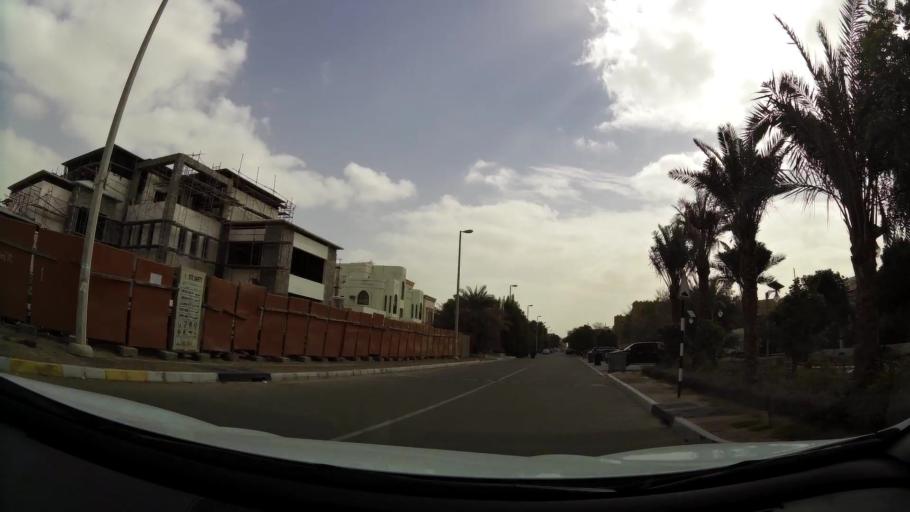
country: AE
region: Abu Dhabi
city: Abu Dhabi
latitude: 24.4094
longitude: 54.4978
